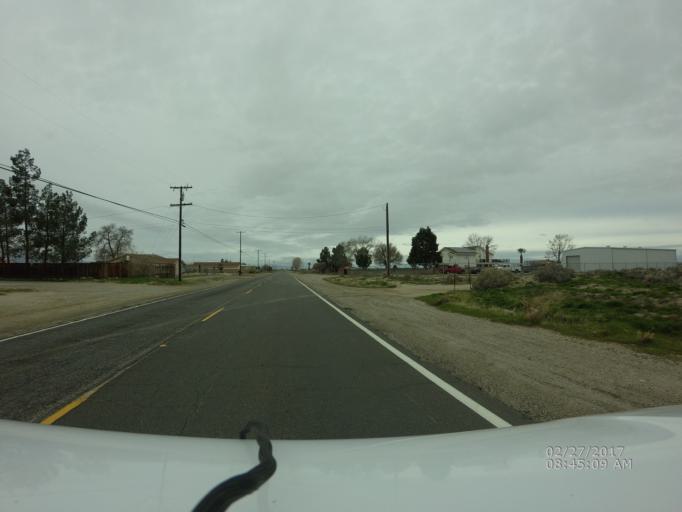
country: US
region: California
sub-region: Los Angeles County
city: Lancaster
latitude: 34.7191
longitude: -118.0725
